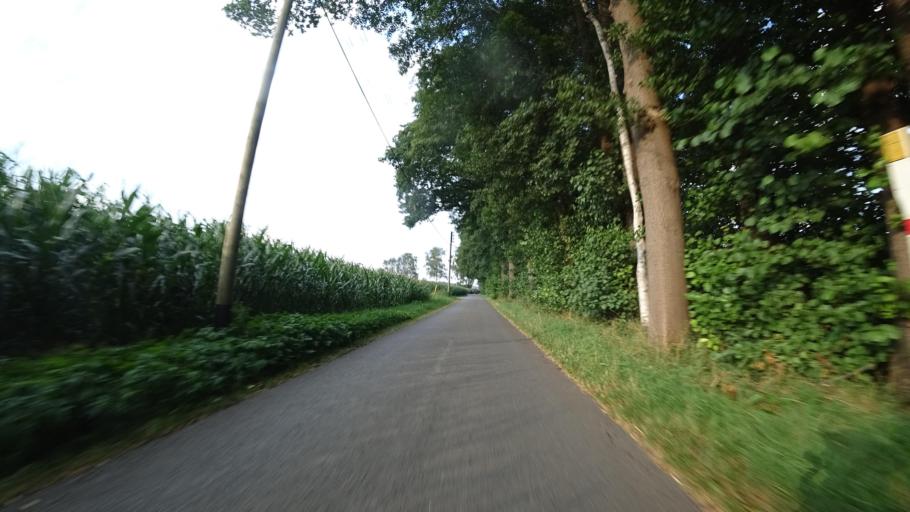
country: DE
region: North Rhine-Westphalia
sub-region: Regierungsbezirk Detmold
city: Steinhagen
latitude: 51.9571
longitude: 8.4373
